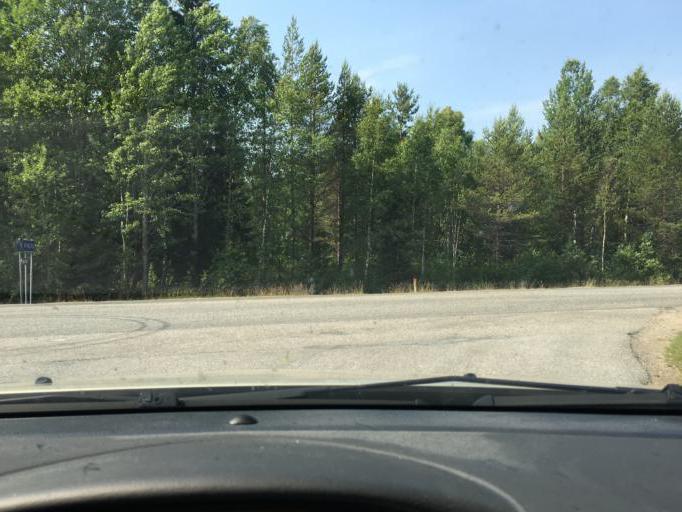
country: SE
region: Norrbotten
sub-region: Kalix Kommun
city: Kalix
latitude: 65.7881
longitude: 23.1754
